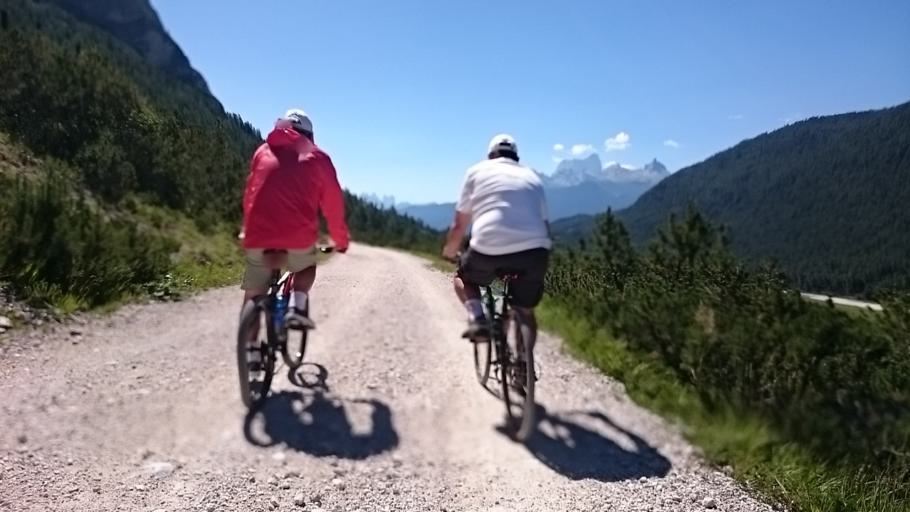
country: IT
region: Veneto
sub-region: Provincia di Belluno
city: Cortina d'Ampezzo
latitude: 46.5834
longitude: 12.1158
